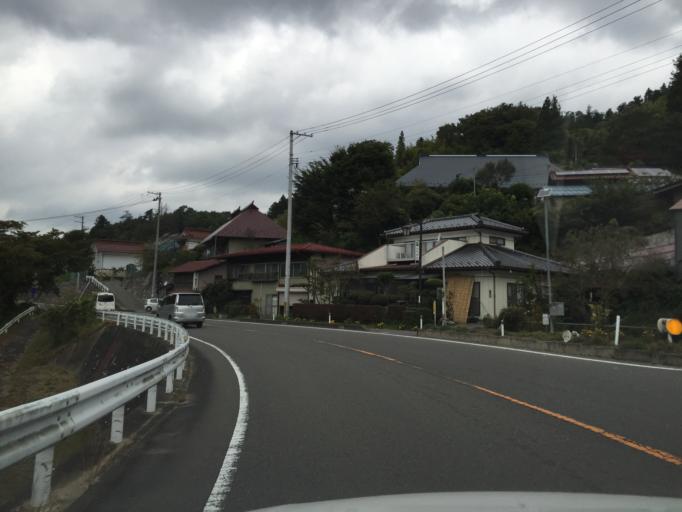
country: JP
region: Fukushima
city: Miharu
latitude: 37.4238
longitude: 140.5265
